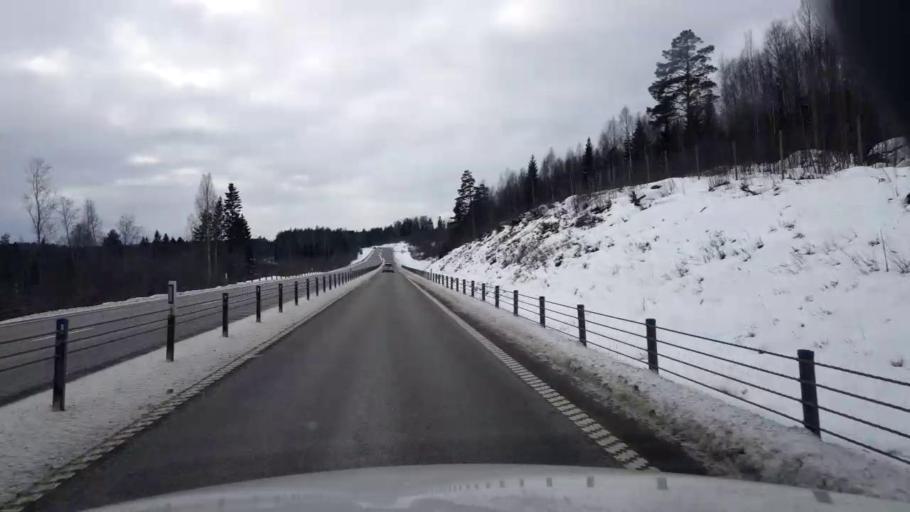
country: SE
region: Vaesternorrland
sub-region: Sundsvalls Kommun
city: Njurundabommen
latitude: 62.0864
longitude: 17.2933
